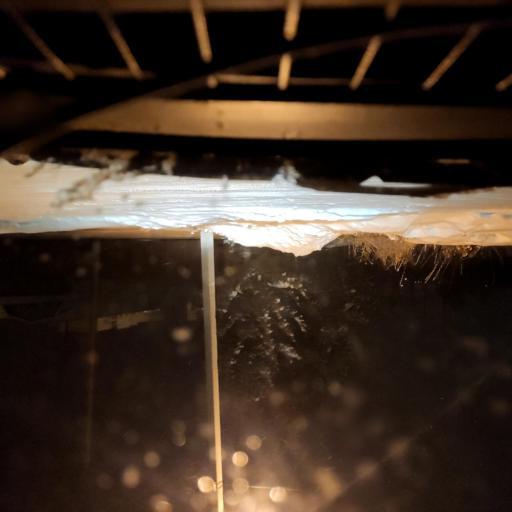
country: RU
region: Perm
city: Lobanovo
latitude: 57.8619
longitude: 56.2751
